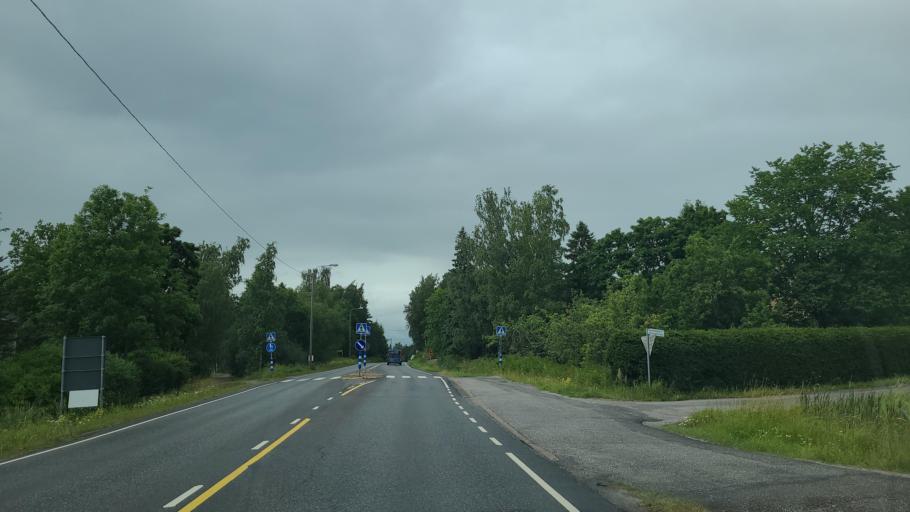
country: FI
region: Varsinais-Suomi
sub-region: Aboland-Turunmaa
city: Kimito
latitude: 60.1691
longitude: 22.7379
